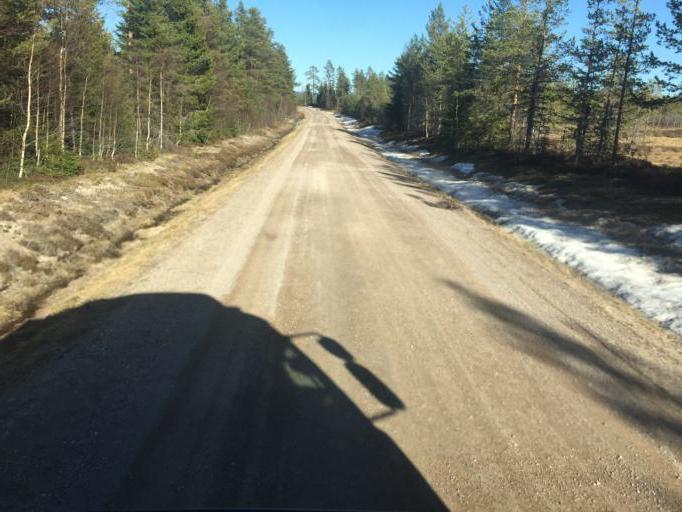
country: SE
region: Vaermland
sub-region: Filipstads Kommun
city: Lesjofors
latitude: 60.2500
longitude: 14.0991
